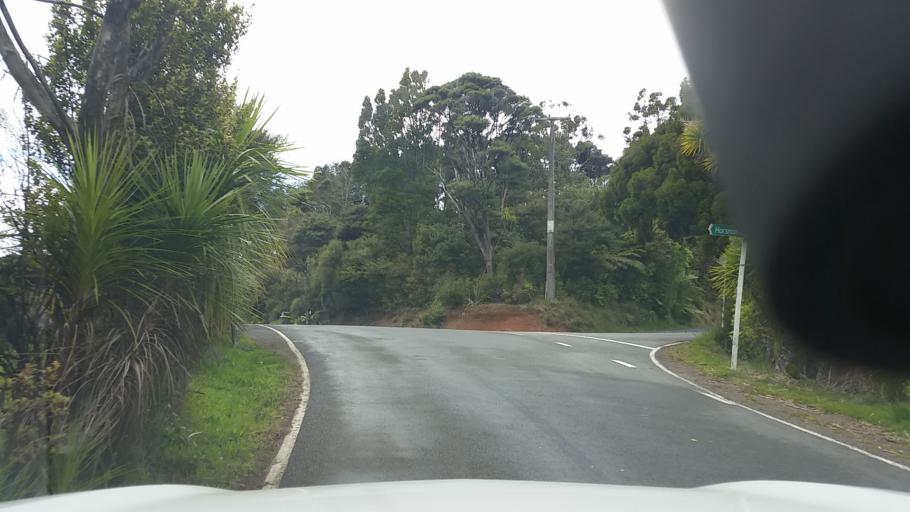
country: NZ
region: Auckland
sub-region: Auckland
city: Muriwai Beach
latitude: -36.8548
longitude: 174.4855
